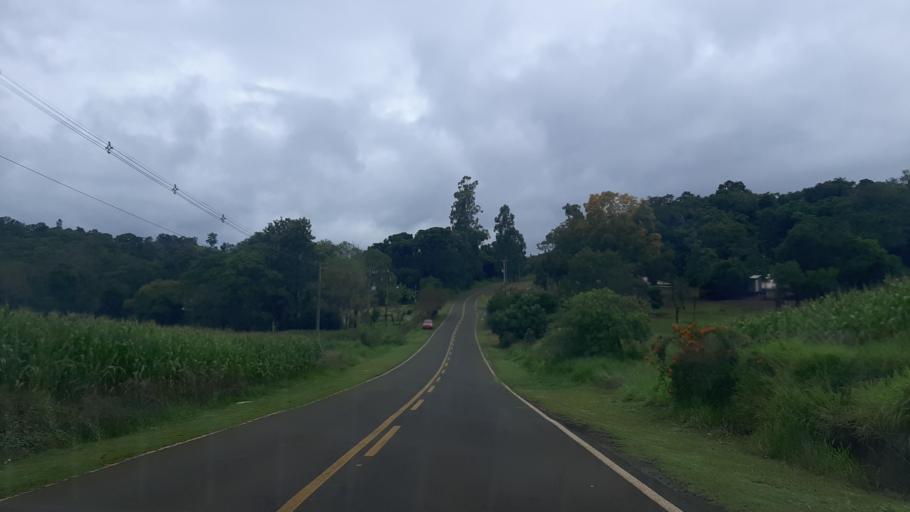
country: BR
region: Parana
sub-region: Ampere
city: Ampere
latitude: -25.9359
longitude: -53.4637
